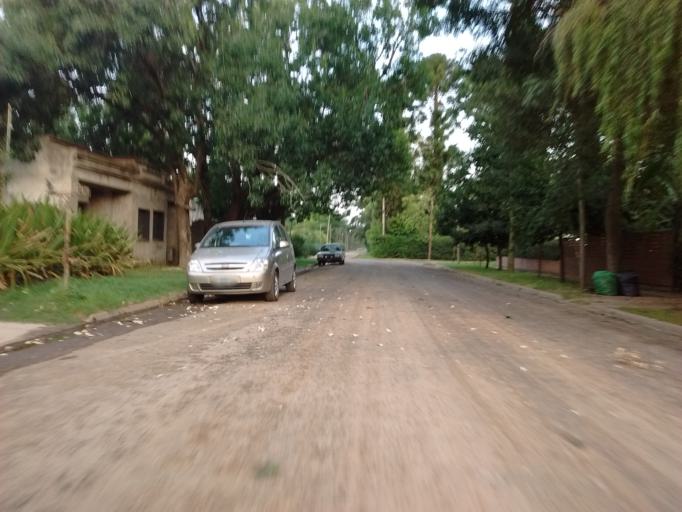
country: AR
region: Santa Fe
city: Funes
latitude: -32.9158
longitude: -60.8038
